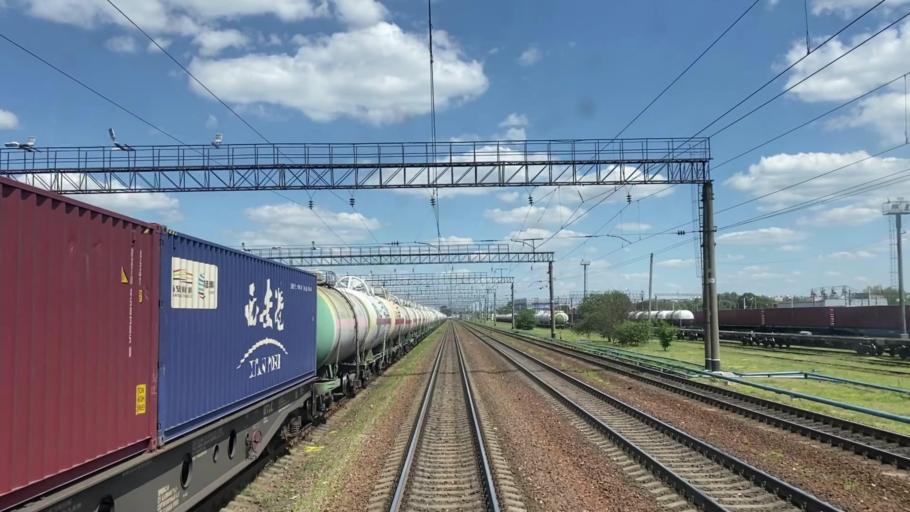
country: BY
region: Brest
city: Brest
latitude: 52.1110
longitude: 23.7311
